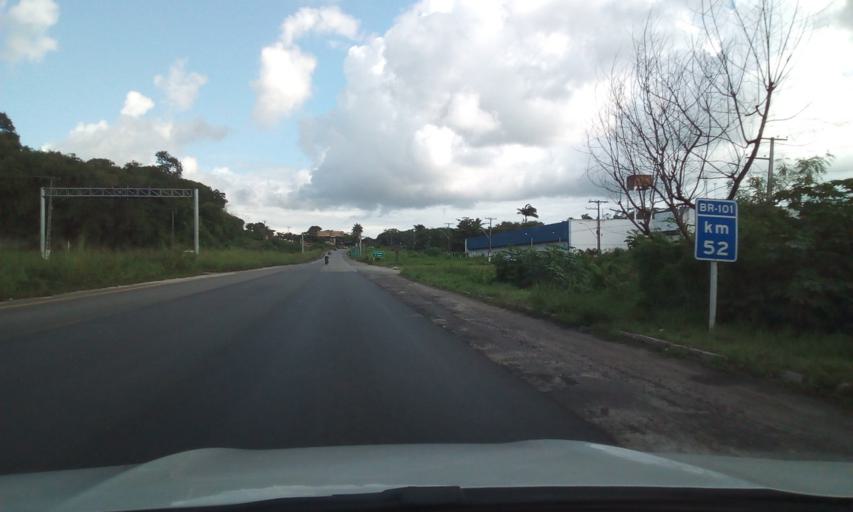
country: BR
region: Pernambuco
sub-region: Abreu E Lima
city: Abreu e Lima
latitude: -7.9242
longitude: -34.8967
